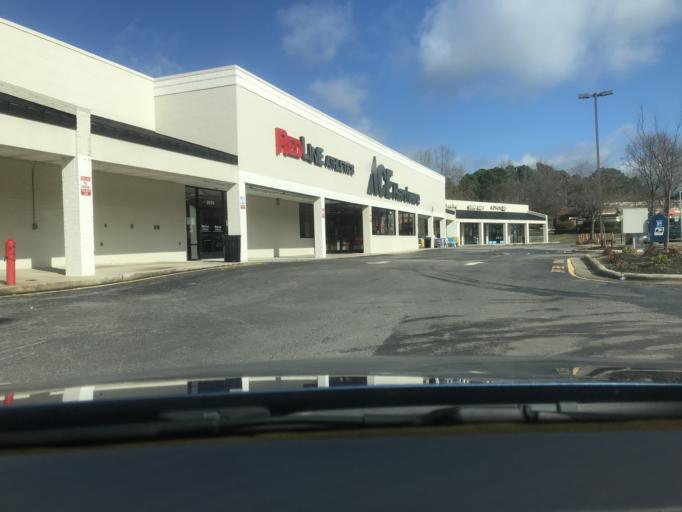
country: US
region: North Carolina
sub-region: Wake County
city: Apex
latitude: 35.7179
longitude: -78.7888
